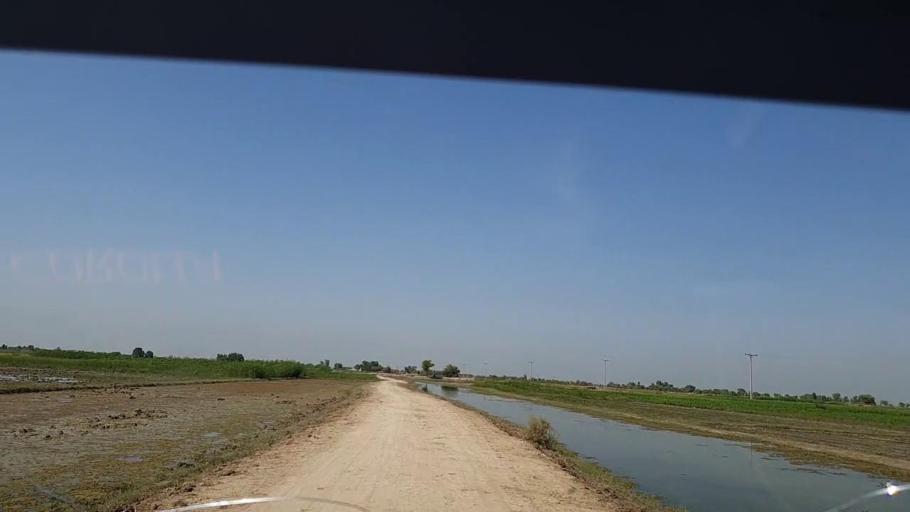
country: PK
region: Sindh
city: Tangwani
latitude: 28.3229
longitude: 69.0868
